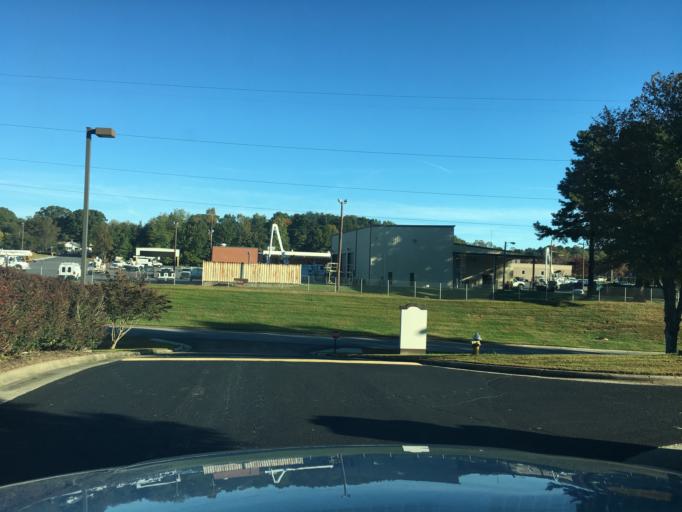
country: US
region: North Carolina
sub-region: Catawba County
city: Hickory
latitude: 35.7316
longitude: -81.3193
